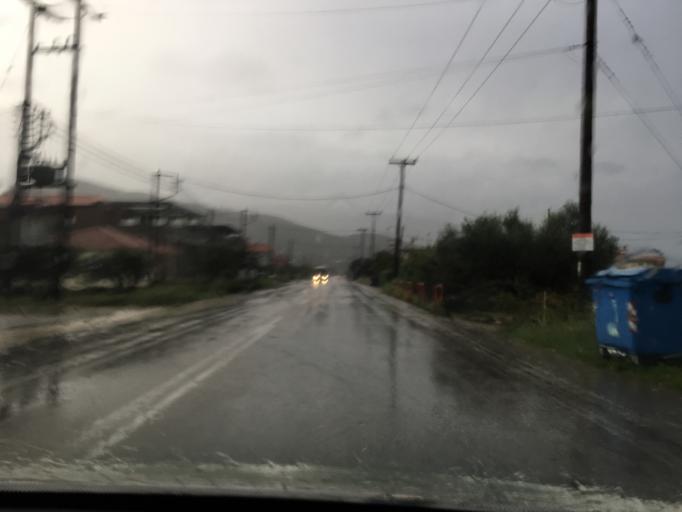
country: GR
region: West Greece
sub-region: Nomos Aitolias kai Akarnanias
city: Antirrio
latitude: 38.3621
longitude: 21.7774
